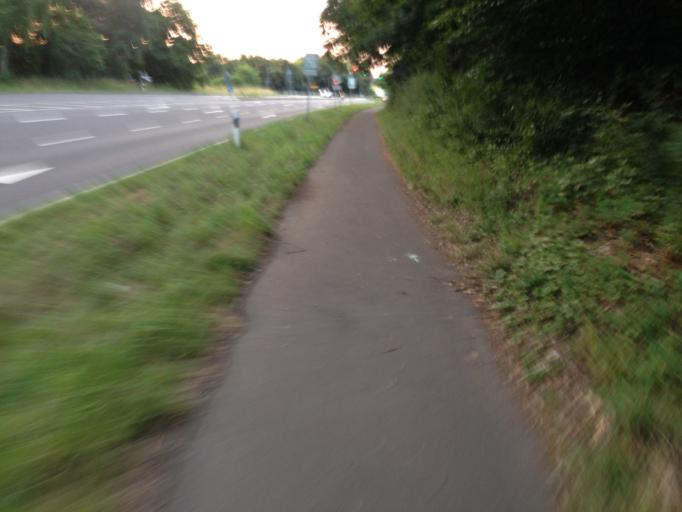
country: DE
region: Hesse
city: Allendorf an der Lahn
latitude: 50.5508
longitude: 8.6468
